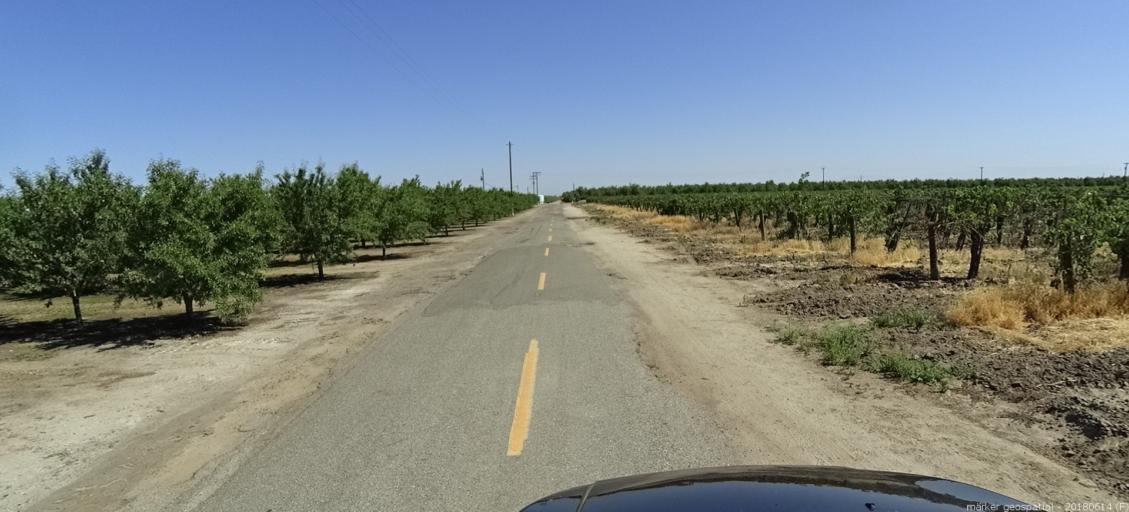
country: US
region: California
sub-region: Madera County
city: Madera
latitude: 36.9802
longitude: -120.1380
